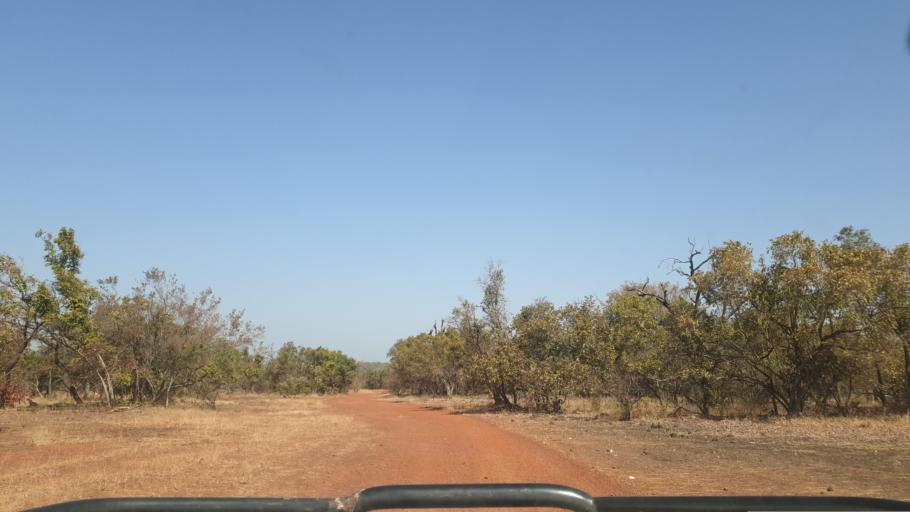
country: ML
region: Koulikoro
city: Dioila
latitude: 11.9187
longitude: -6.9839
